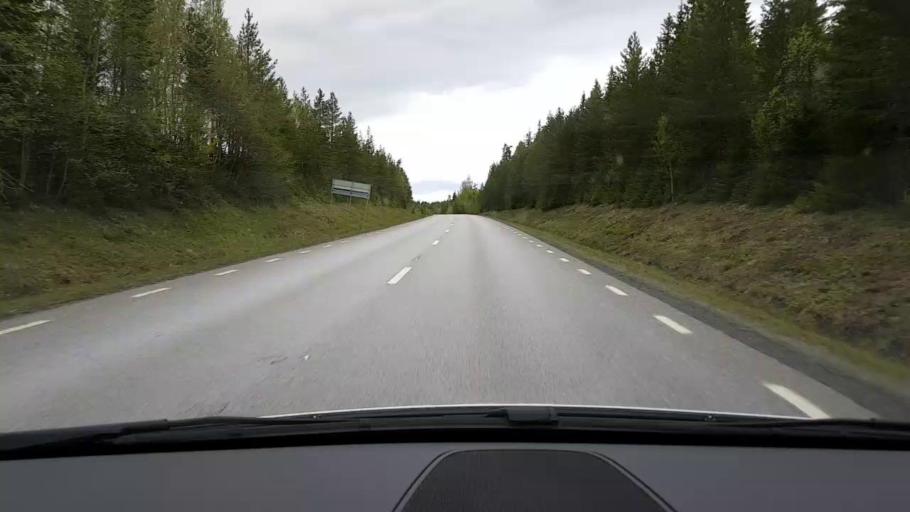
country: SE
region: Jaemtland
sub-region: Krokoms Kommun
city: Valla
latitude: 63.2996
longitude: 13.9265
